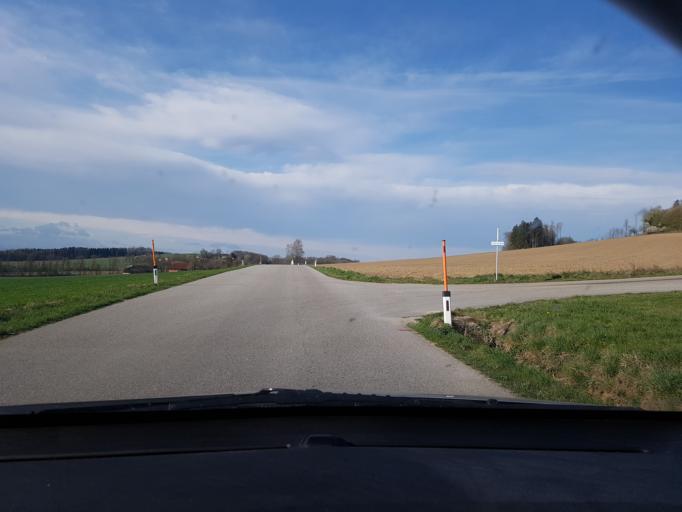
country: AT
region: Upper Austria
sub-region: Politischer Bezirk Linz-Land
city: Sankt Florian
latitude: 48.1604
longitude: 14.3972
